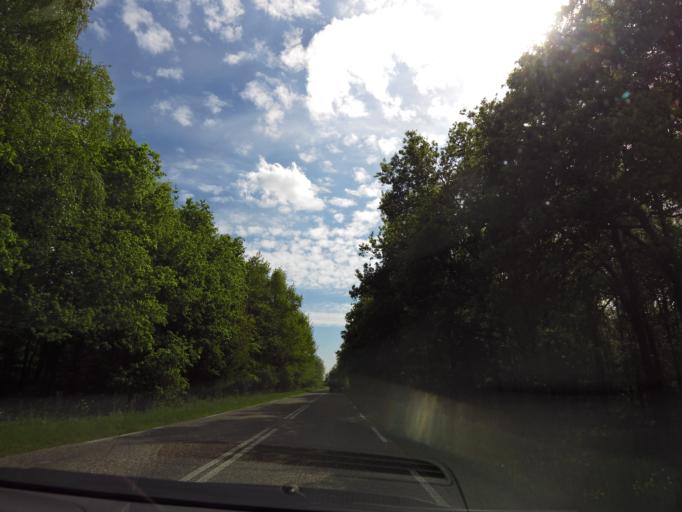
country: NL
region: Limburg
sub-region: Gemeente Leudal
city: Haelen
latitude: 51.2779
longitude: 5.9788
